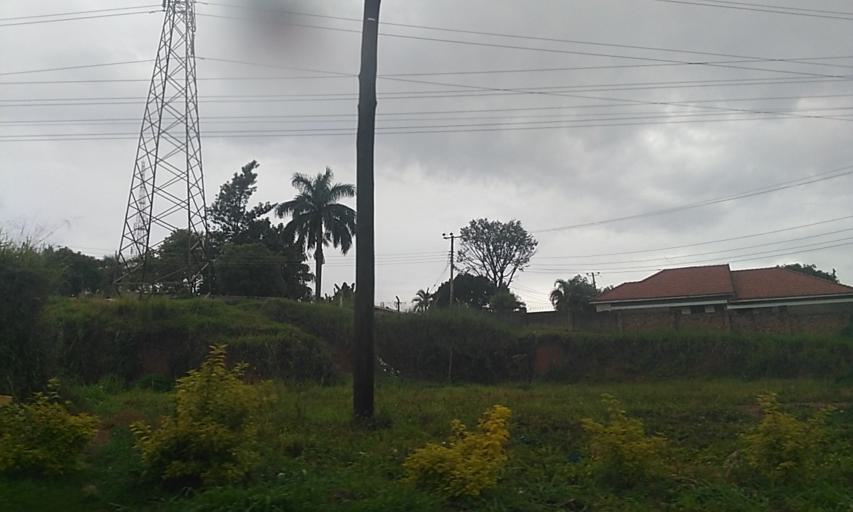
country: UG
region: Central Region
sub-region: Wakiso District
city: Kireka
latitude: 0.3400
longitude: 32.6297
